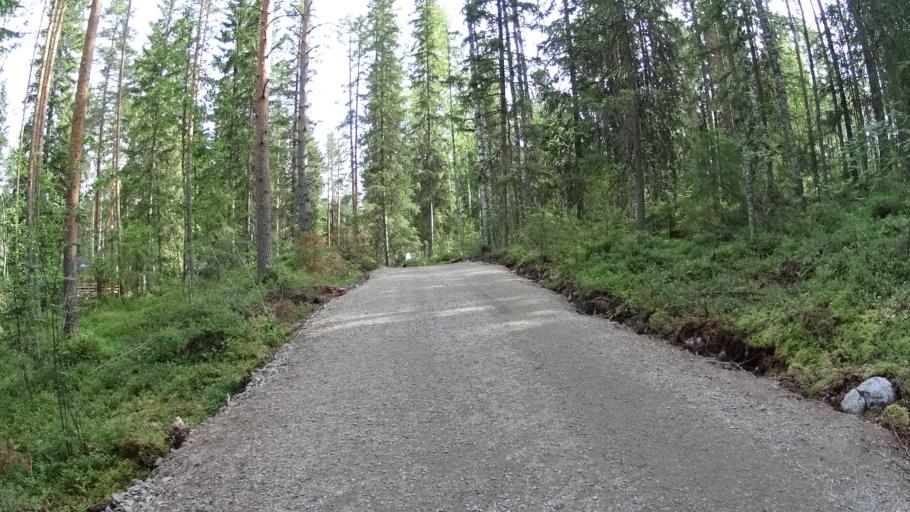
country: FI
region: Southern Ostrobothnia
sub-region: Kuusiokunnat
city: AEhtaeri
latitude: 62.5381
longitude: 24.1833
